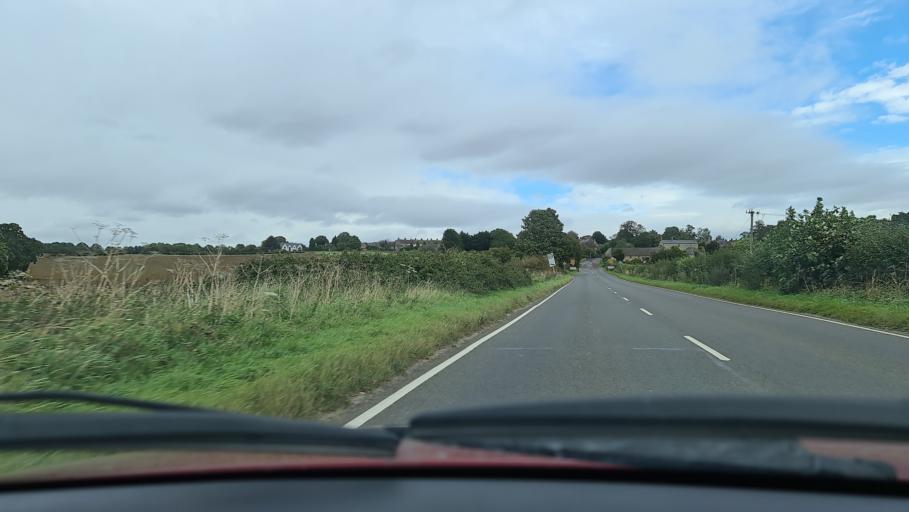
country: GB
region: England
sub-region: Oxfordshire
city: Somerton
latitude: 51.9974
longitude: -1.2611
